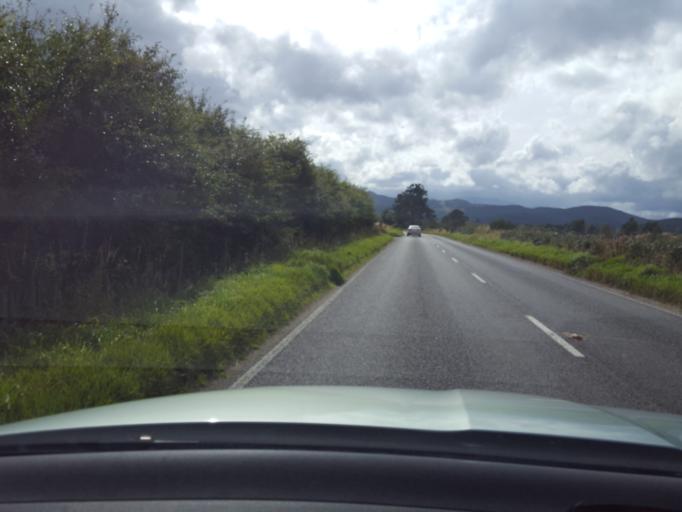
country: GB
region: Scotland
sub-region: Aberdeenshire
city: Ballater
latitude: 57.0572
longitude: -3.0246
